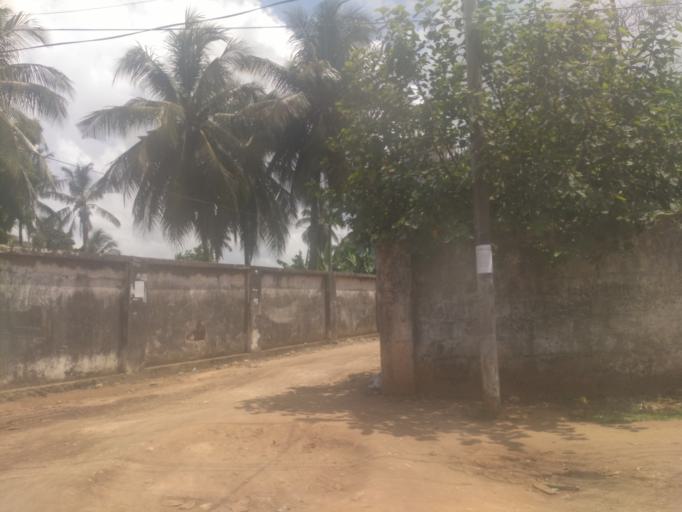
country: TZ
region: Zanzibar Urban/West
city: Zanzibar
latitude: -6.2136
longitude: 39.2113
